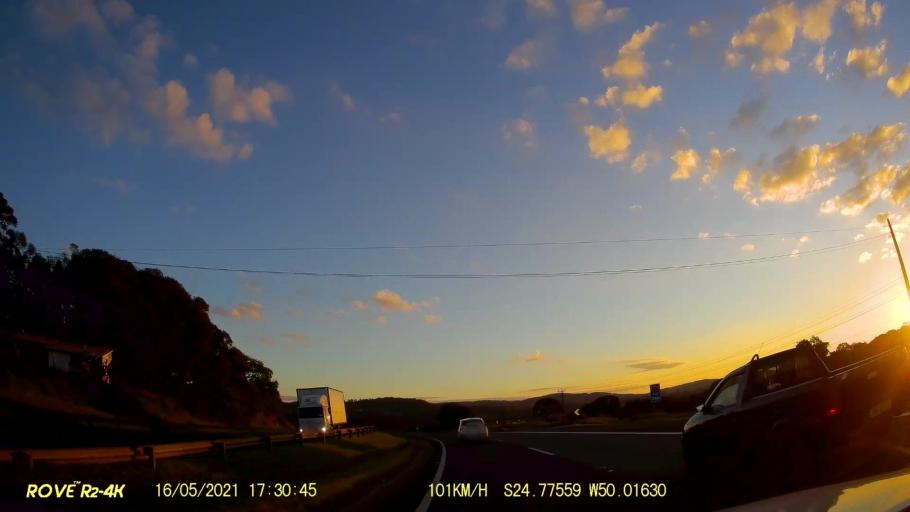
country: BR
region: Parana
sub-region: Castro
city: Castro
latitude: -24.7758
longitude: -50.0167
